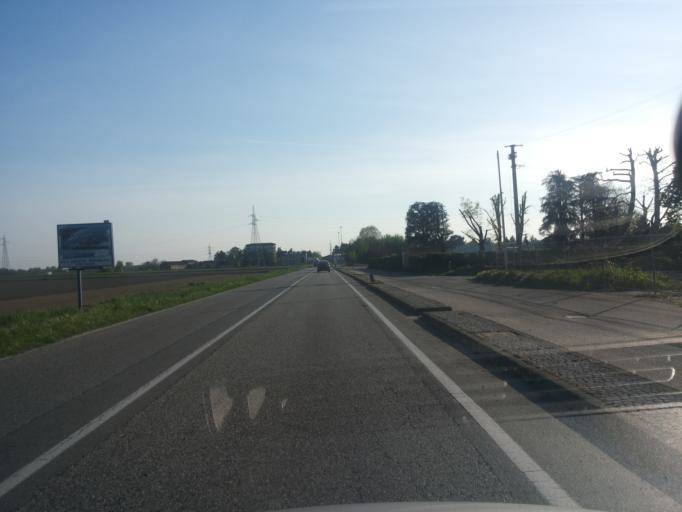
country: IT
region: Lombardy
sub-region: Provincia di Pavia
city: Castello d'Agogna
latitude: 45.2395
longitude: 8.6971
